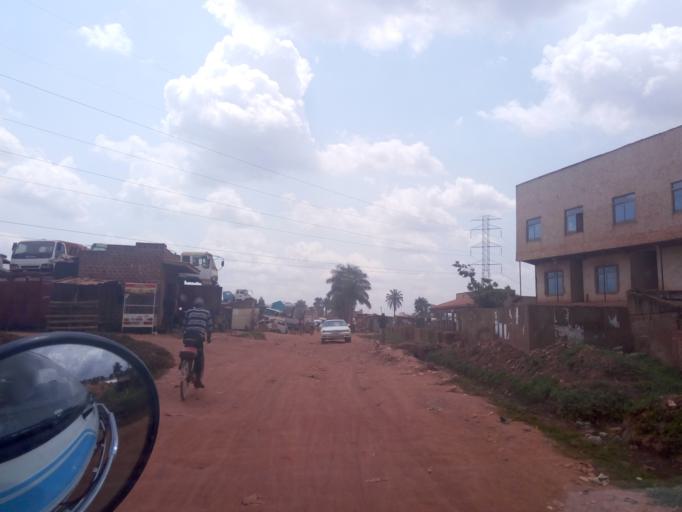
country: UG
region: Central Region
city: Kampala Central Division
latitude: 0.3462
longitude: 32.5579
